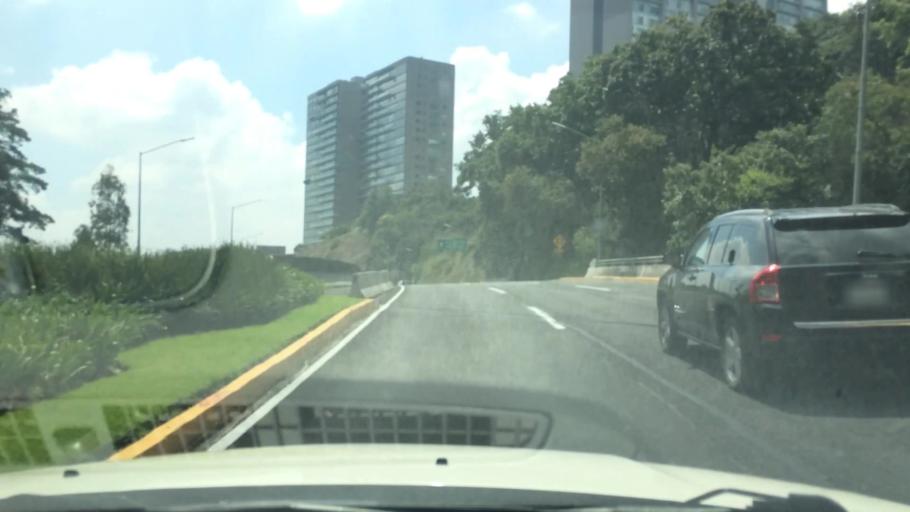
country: MX
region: Mexico City
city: Magdalena Contreras
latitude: 19.3369
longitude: -99.2406
